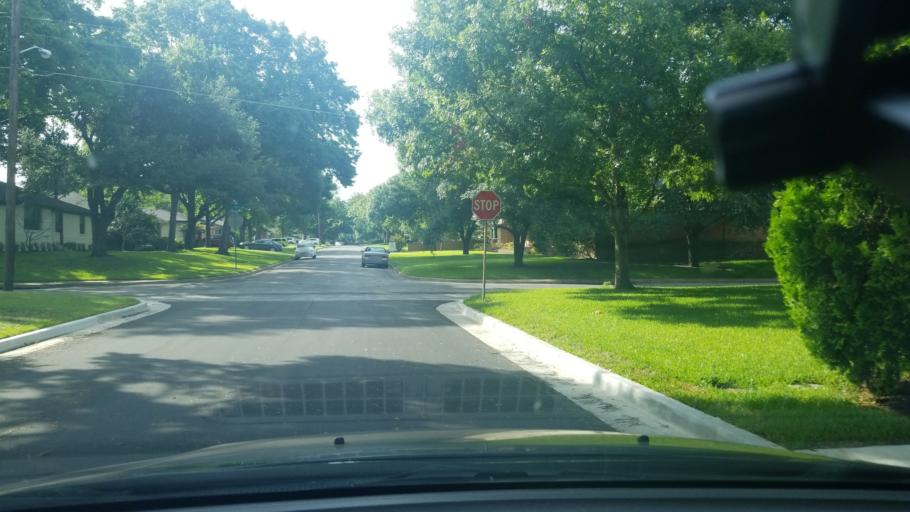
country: US
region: Texas
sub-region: Dallas County
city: Highland Park
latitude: 32.8030
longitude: -96.7041
